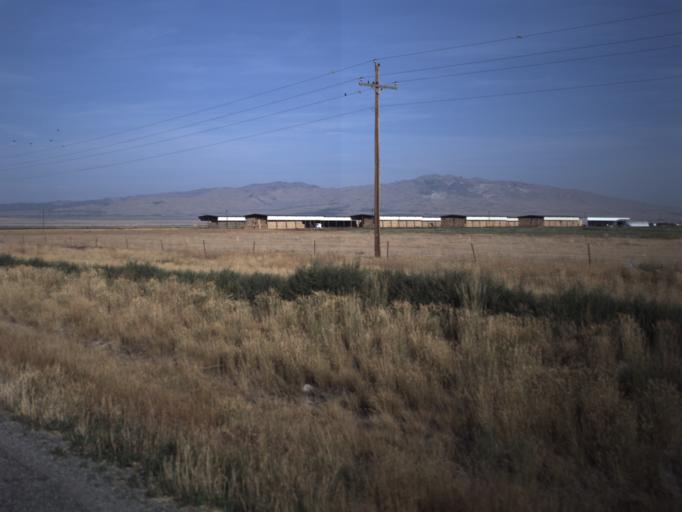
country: US
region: Idaho
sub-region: Oneida County
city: Malad City
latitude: 41.9667
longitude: -112.8975
